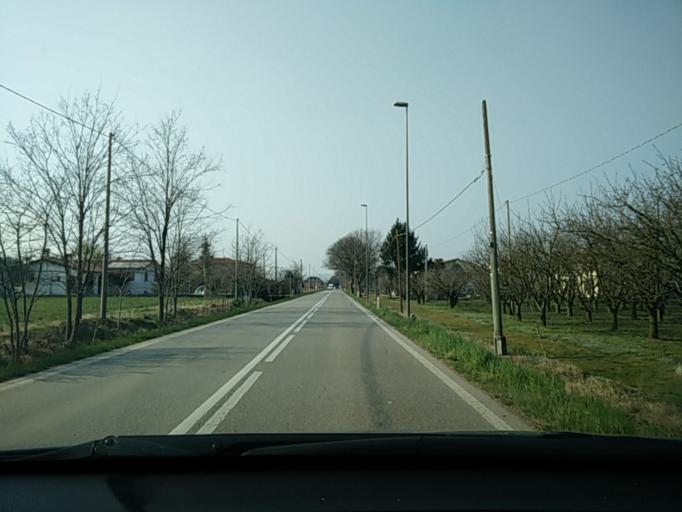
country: IT
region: Veneto
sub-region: Provincia di Treviso
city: Santandra
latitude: 45.7352
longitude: 12.1857
